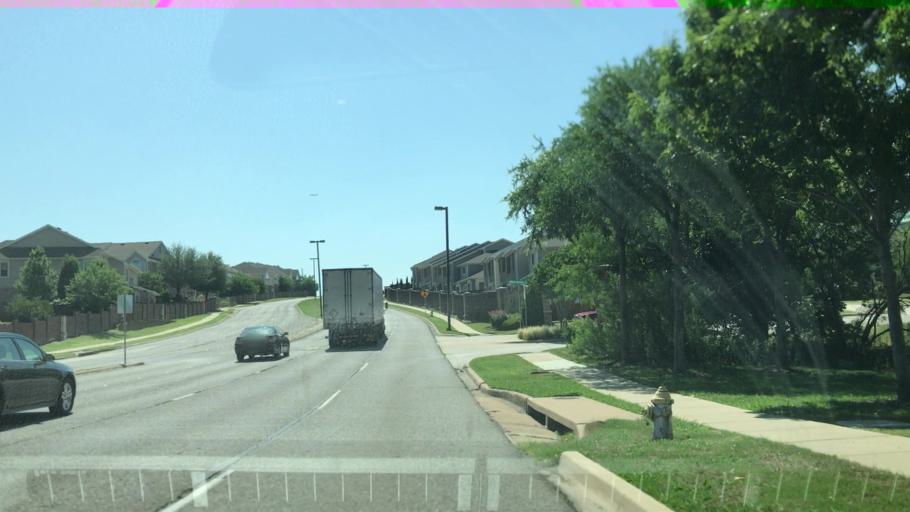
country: US
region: Texas
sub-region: Dallas County
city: Irving
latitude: 32.8657
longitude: -96.9960
